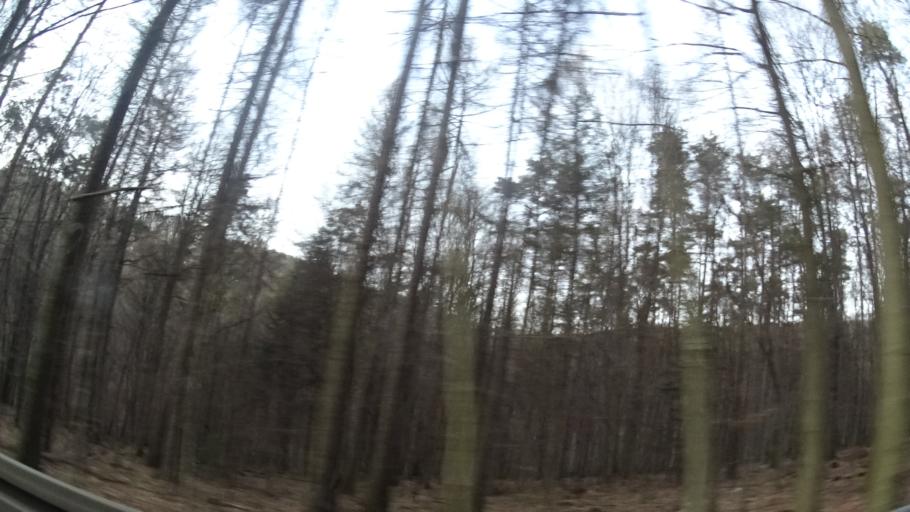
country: DE
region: Bavaria
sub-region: Regierungsbezirk Unterfranken
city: Mombris
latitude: 50.0899
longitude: 9.1647
